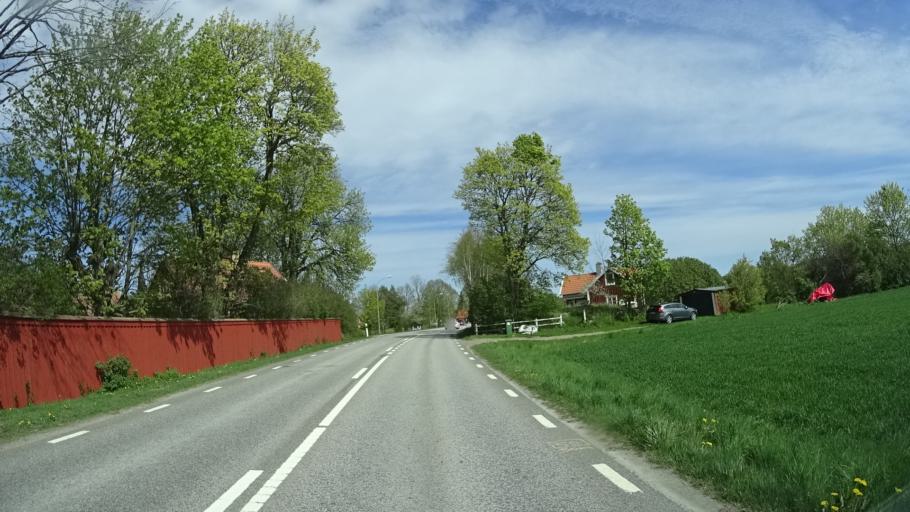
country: SE
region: OEstergoetland
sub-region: Mjolby Kommun
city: Mantorp
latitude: 58.3654
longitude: 15.3101
